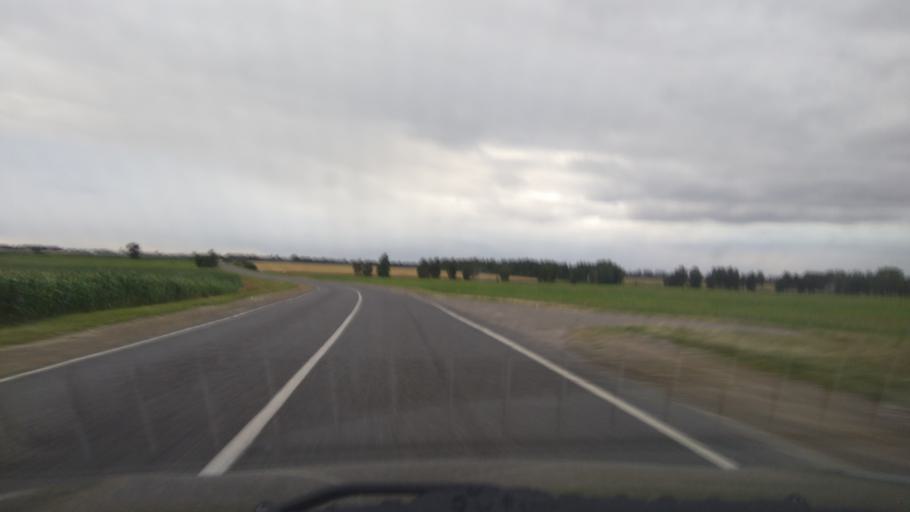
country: BY
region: Brest
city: Byaroza
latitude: 52.4345
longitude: 24.9802
